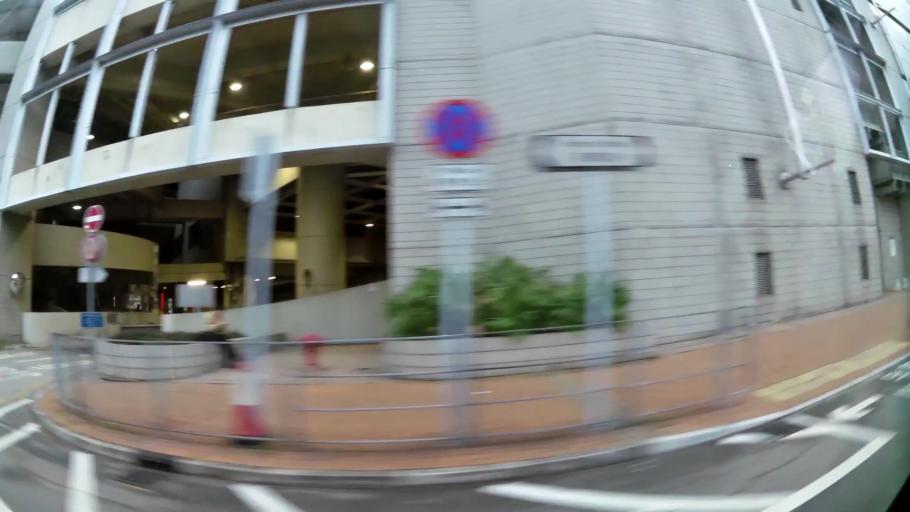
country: HK
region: Tsuen Wan
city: Tsuen Wan
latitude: 22.3582
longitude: 114.1057
